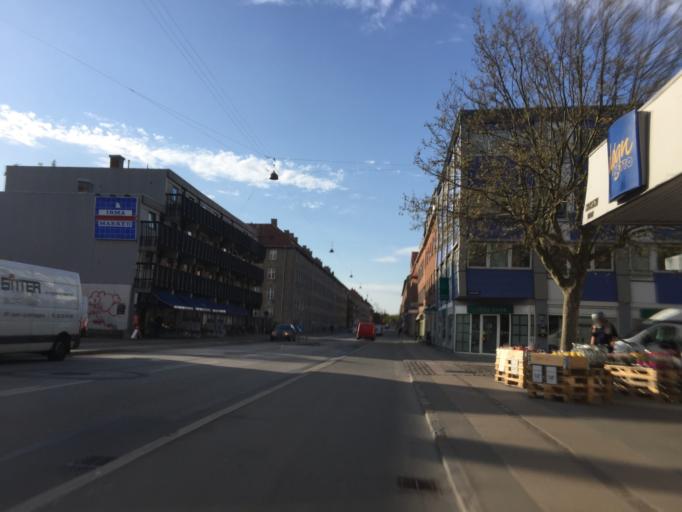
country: DK
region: Capital Region
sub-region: Kobenhavn
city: Vanlose
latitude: 55.6886
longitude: 12.4894
